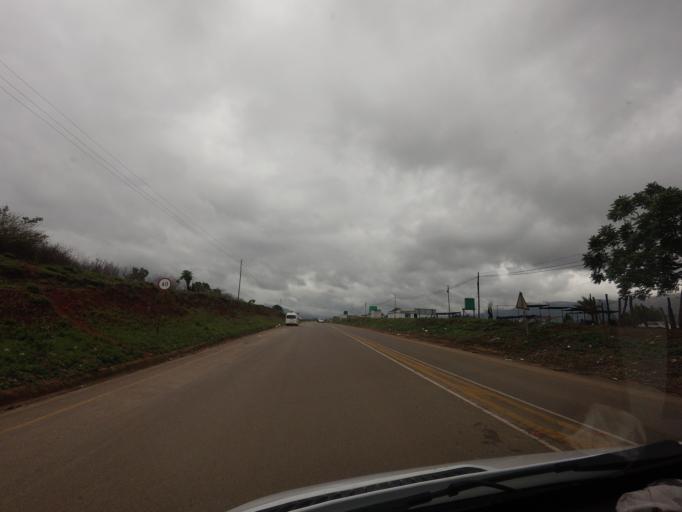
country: SZ
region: Hhohho
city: Lobamba
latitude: -26.4904
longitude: 31.2250
